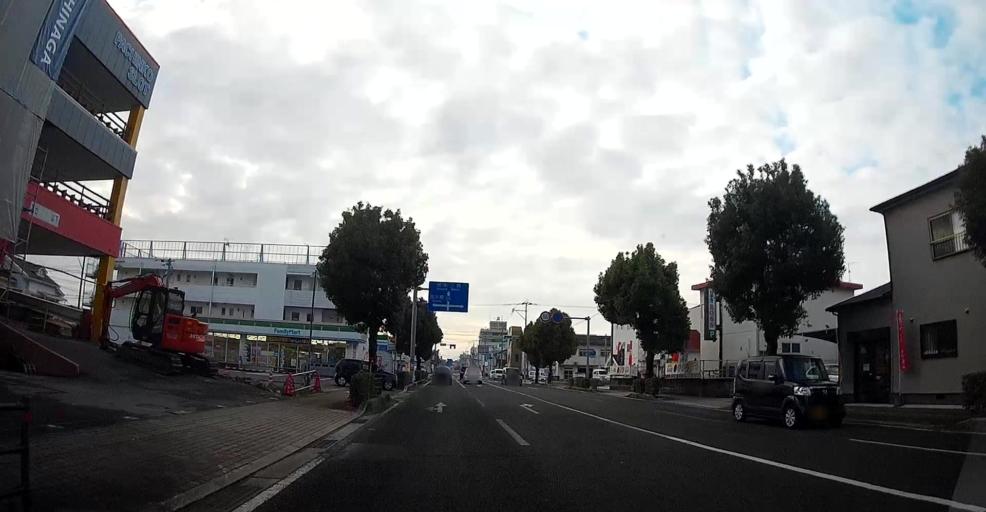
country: JP
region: Kumamoto
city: Hondo
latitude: 32.4605
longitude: 130.1918
